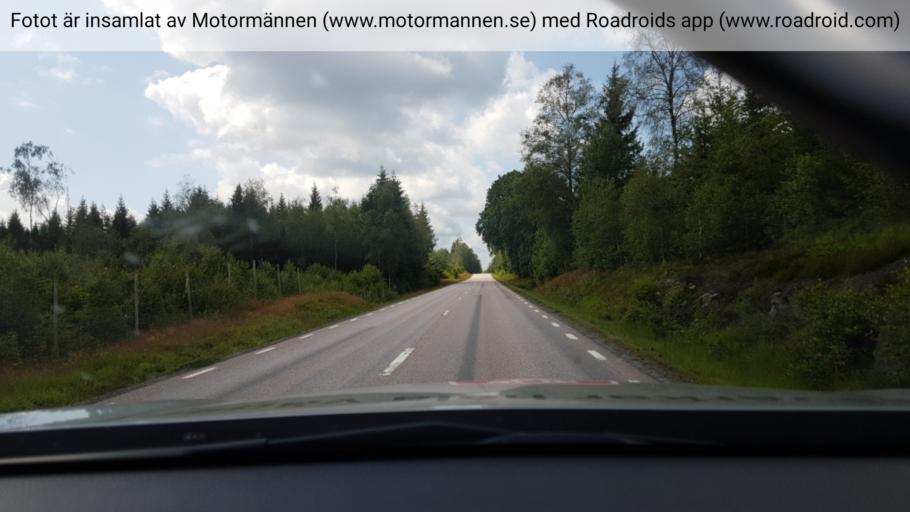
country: SE
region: Vaestra Goetaland
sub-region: Svenljunga Kommun
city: Svenljunga
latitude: 57.4880
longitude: 12.9963
